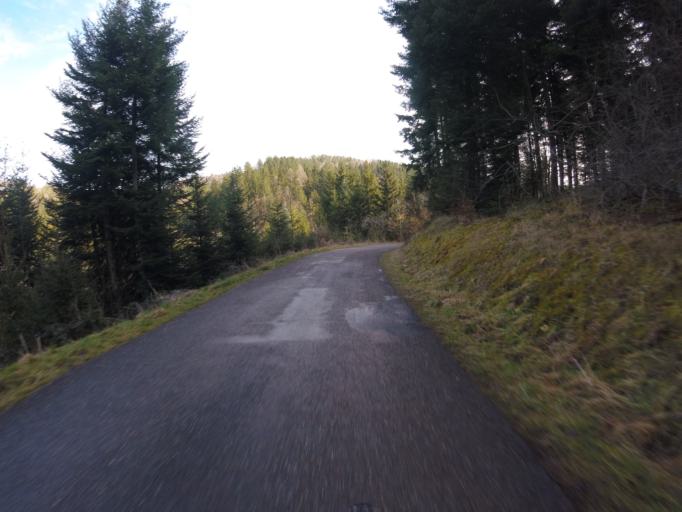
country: DE
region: Baden-Wuerttemberg
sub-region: Regierungsbezirk Stuttgart
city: Murrhardt
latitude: 48.9819
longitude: 9.6076
